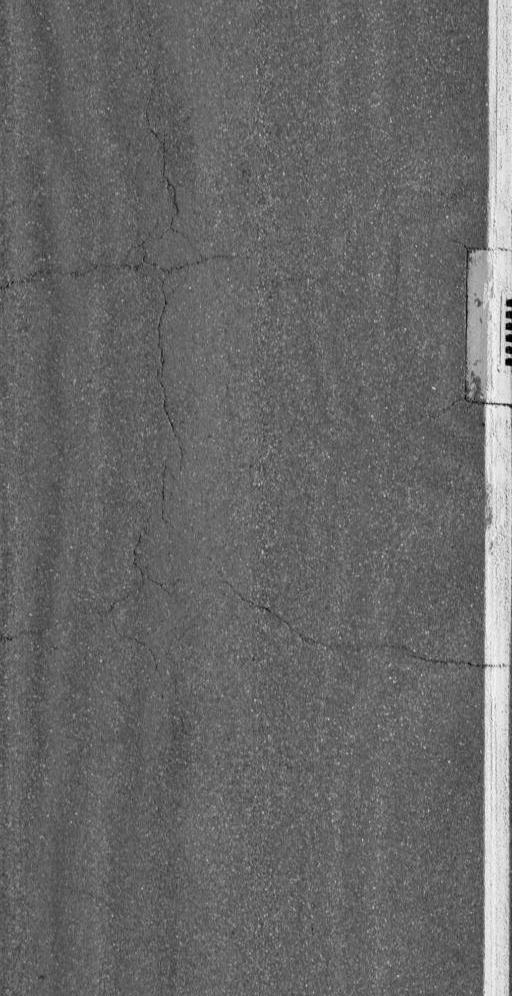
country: US
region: Vermont
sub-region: Windham County
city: Brattleboro
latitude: 42.8867
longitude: -72.5603
